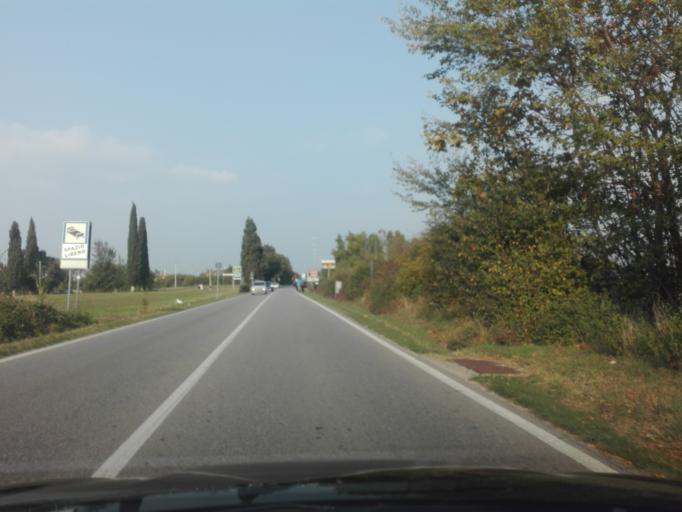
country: IT
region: Veneto
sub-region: Provincia di Verona
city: Cavalcaselle
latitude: 45.4499
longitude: 10.7123
